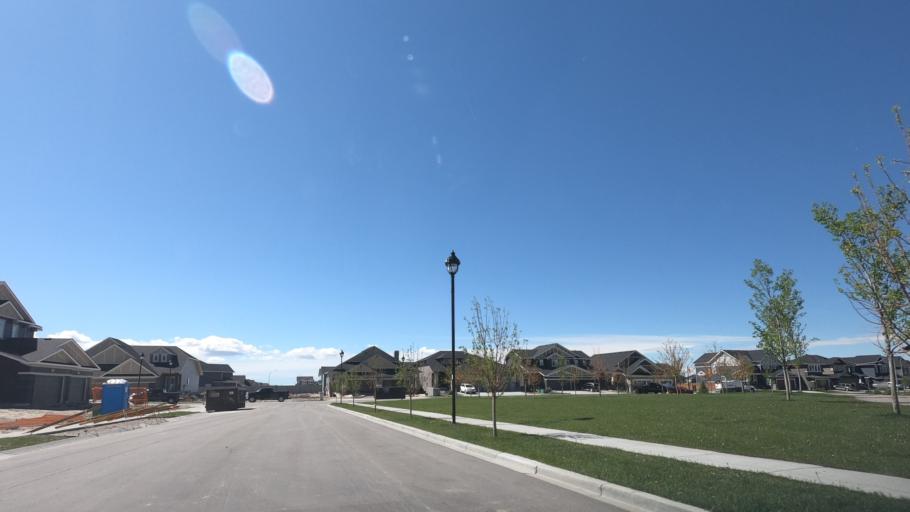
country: CA
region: Alberta
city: Airdrie
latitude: 51.2661
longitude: -113.9708
